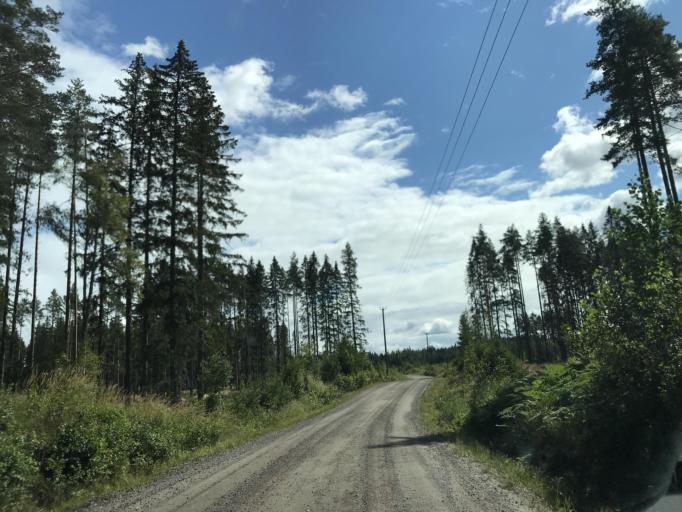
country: FI
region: Uusimaa
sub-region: Helsinki
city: Kaerkoelae
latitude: 60.6372
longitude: 23.8265
